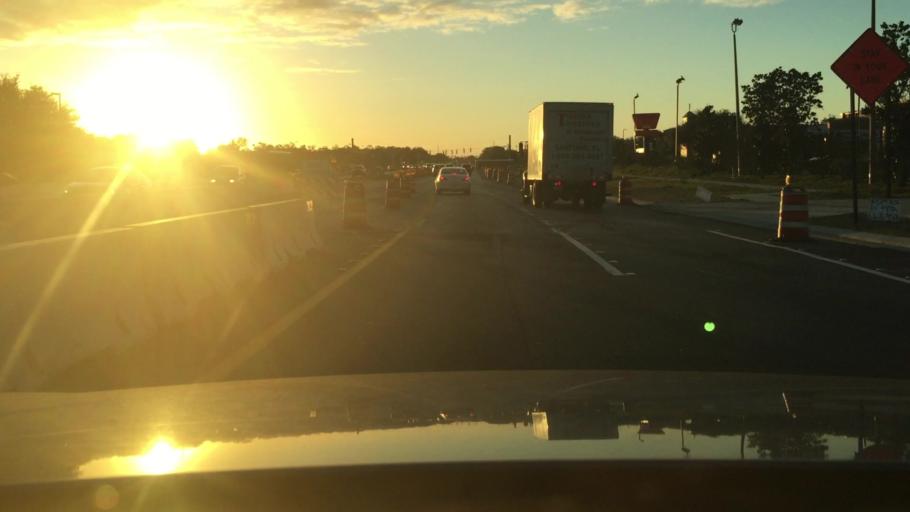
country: US
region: Florida
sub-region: Osceola County
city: Saint Cloud
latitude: 28.2564
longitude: -81.3212
